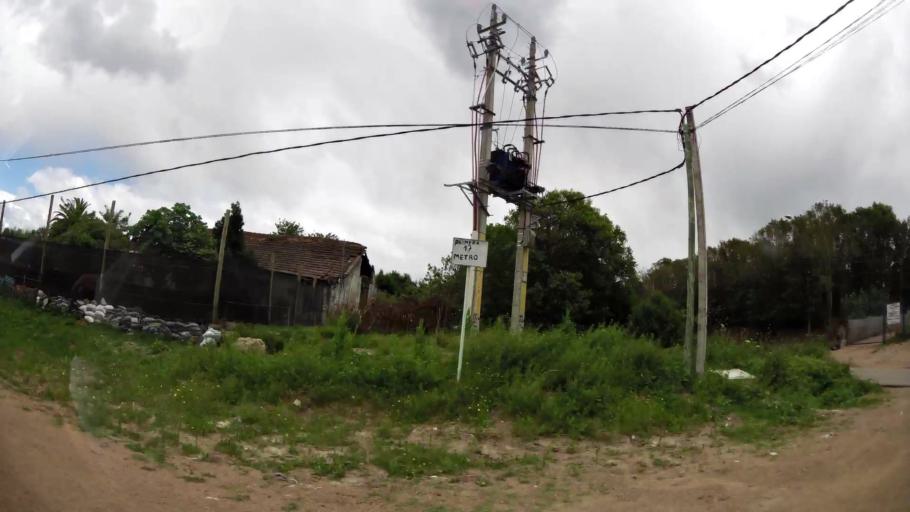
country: UY
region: Canelones
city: Toledo
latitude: -34.8021
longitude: -56.1316
